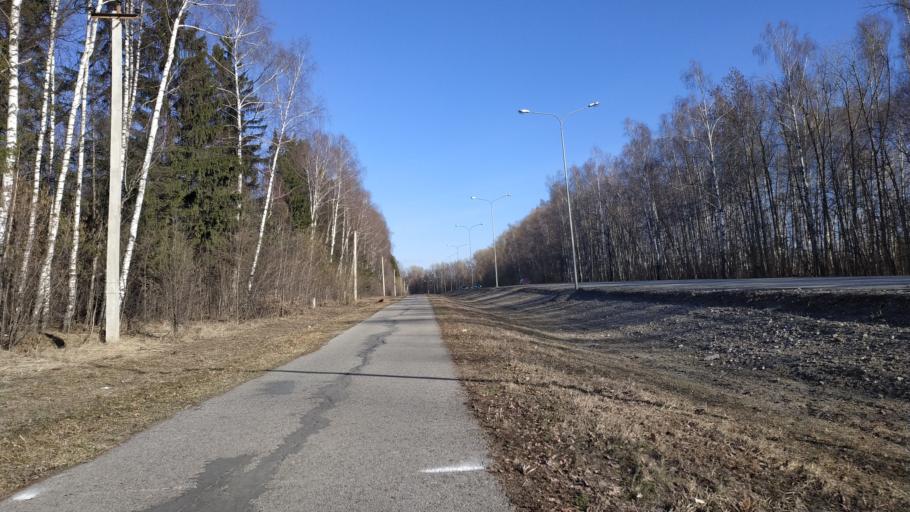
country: RU
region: Chuvashia
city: Novyye Lapsary
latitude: 56.1305
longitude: 47.1148
